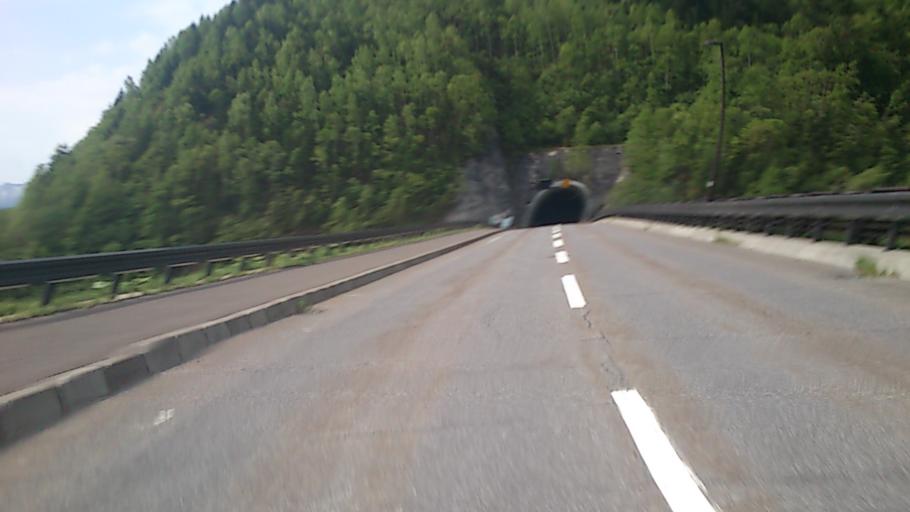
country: JP
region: Hokkaido
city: Kamikawa
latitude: 43.6761
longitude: 143.0363
